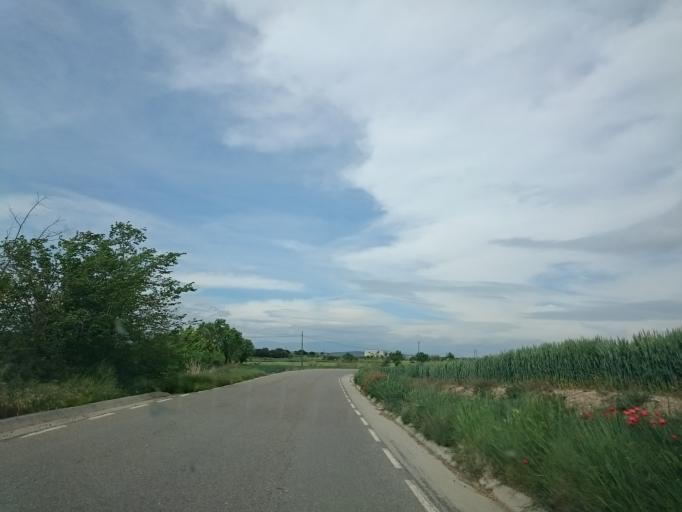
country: ES
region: Catalonia
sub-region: Provincia de Lleida
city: Ivorra
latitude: 41.7902
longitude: 1.3010
